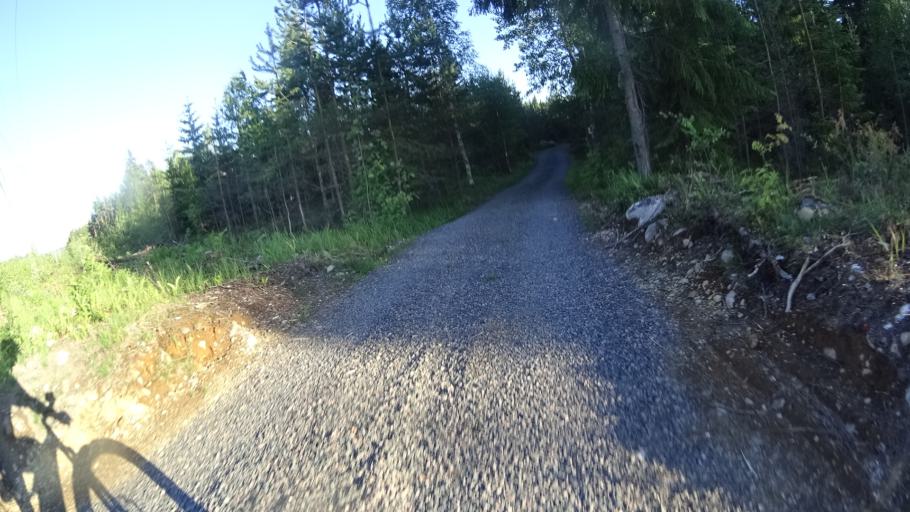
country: FI
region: Uusimaa
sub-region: Helsinki
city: Karkkila
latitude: 60.5940
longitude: 24.1050
